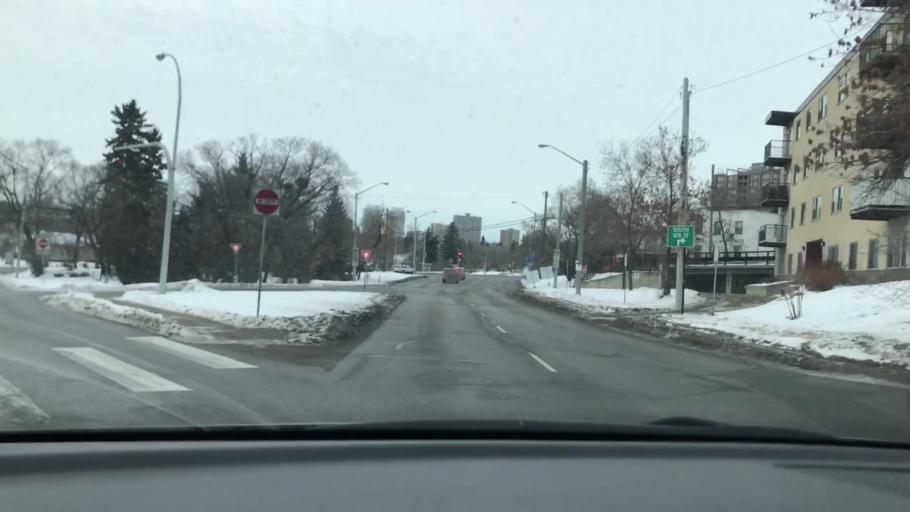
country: CA
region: Alberta
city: Edmonton
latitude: 53.5351
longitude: -113.4974
